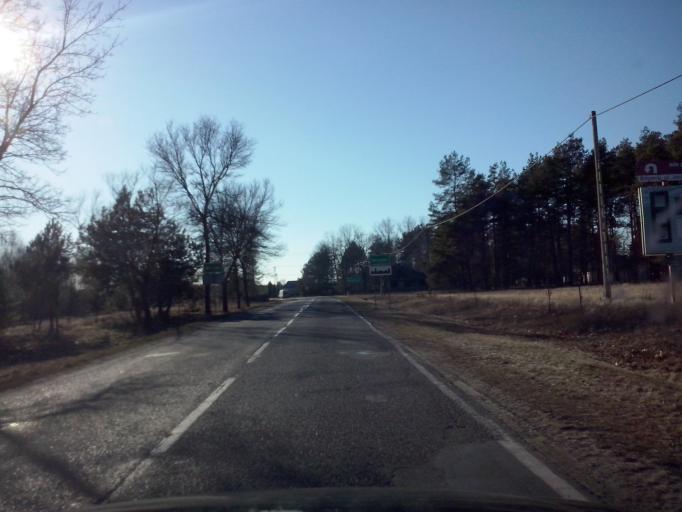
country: PL
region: Subcarpathian Voivodeship
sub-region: Powiat nizanski
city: Harasiuki
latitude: 50.4850
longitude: 22.4813
